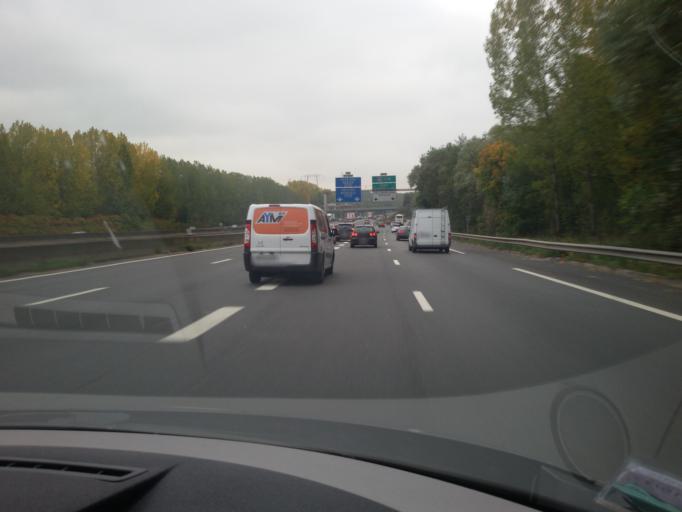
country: FR
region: Ile-de-France
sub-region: Departement de l'Essonne
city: Les Ulis
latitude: 48.6610
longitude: 2.1856
